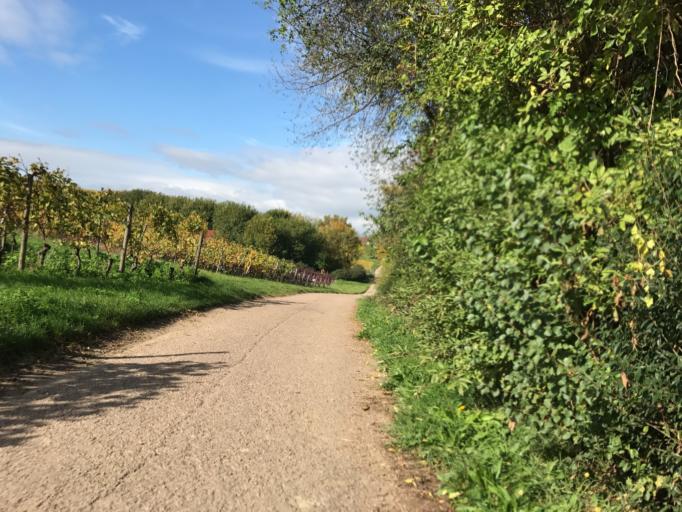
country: DE
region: Rheinland-Pfalz
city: Gau-Algesheim
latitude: 49.9465
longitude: 8.0142
